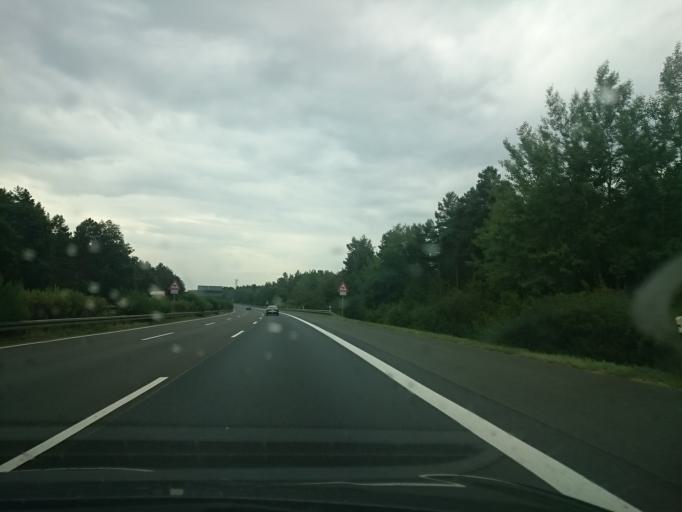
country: DE
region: Brandenburg
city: Fichtenwalde
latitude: 52.2624
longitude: 12.9070
